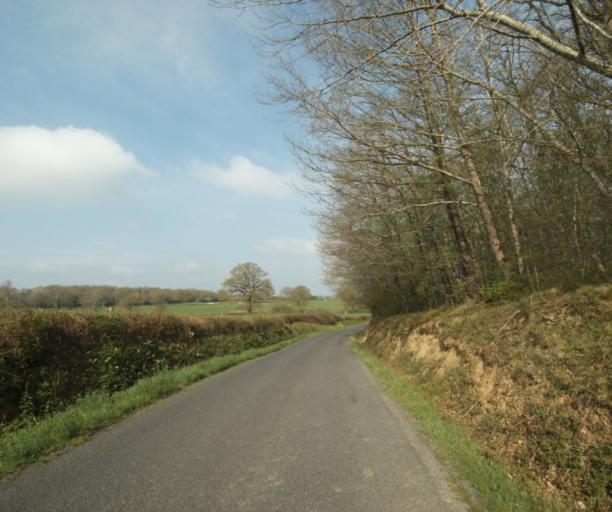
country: FR
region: Bourgogne
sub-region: Departement de Saone-et-Loire
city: Paray-le-Monial
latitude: 46.4276
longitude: 4.1803
